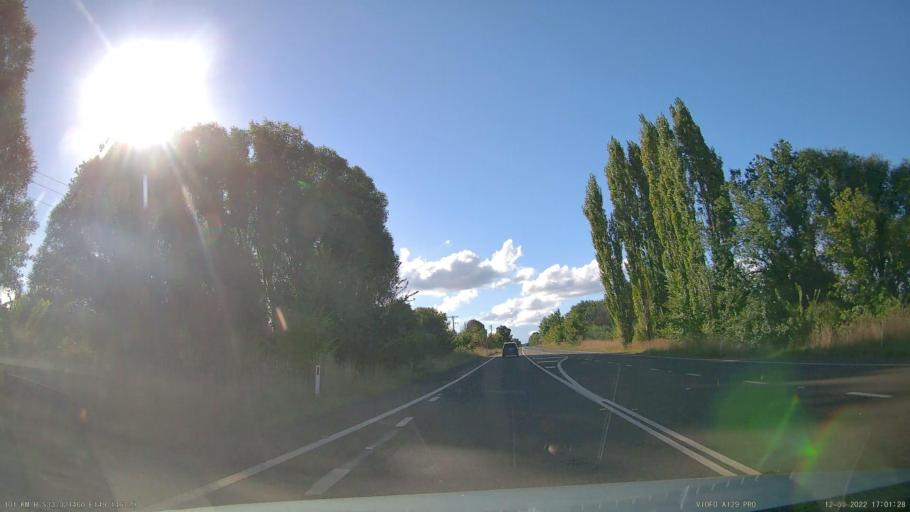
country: AU
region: New South Wales
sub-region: Orange Municipality
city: Orange
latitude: -33.3212
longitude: 149.1466
